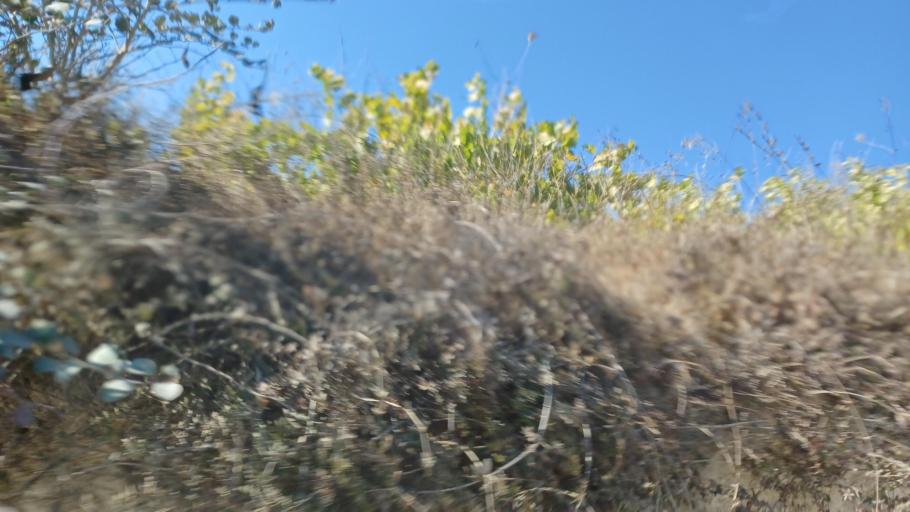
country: CY
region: Pafos
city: Mesogi
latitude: 34.8689
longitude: 32.5248
